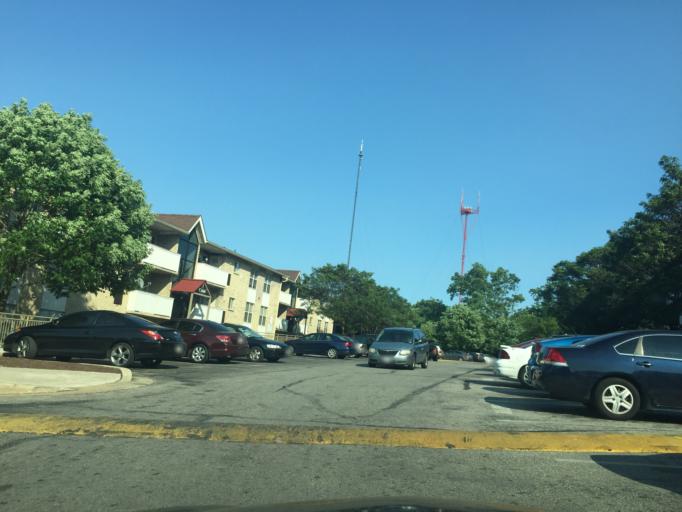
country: US
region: Maryland
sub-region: Baltimore County
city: Lochearn
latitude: 39.3400
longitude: -76.6592
